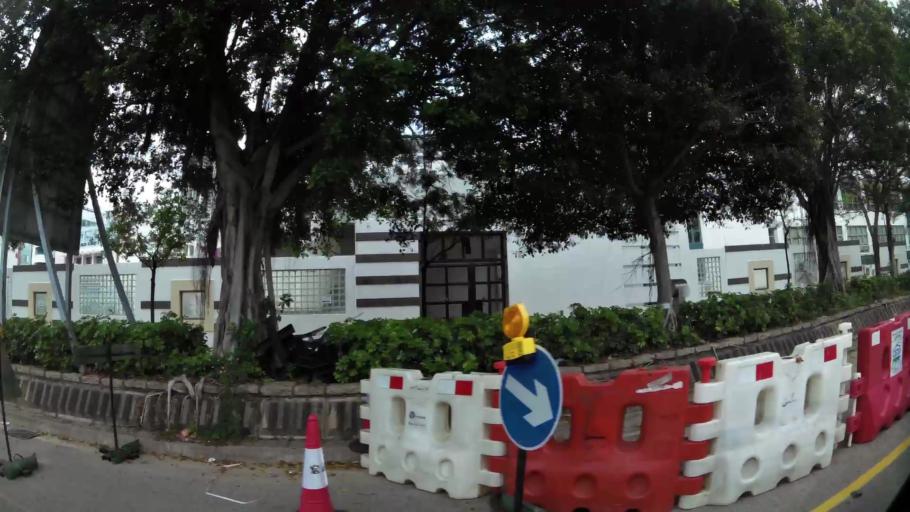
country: HK
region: Sham Shui Po
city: Sham Shui Po
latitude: 22.3296
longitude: 114.1520
